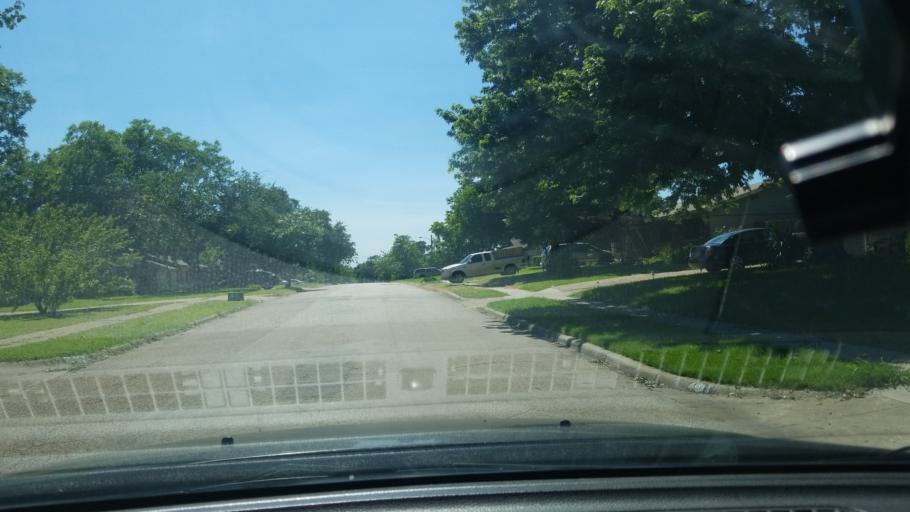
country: US
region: Texas
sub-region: Dallas County
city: Mesquite
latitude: 32.7754
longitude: -96.6027
